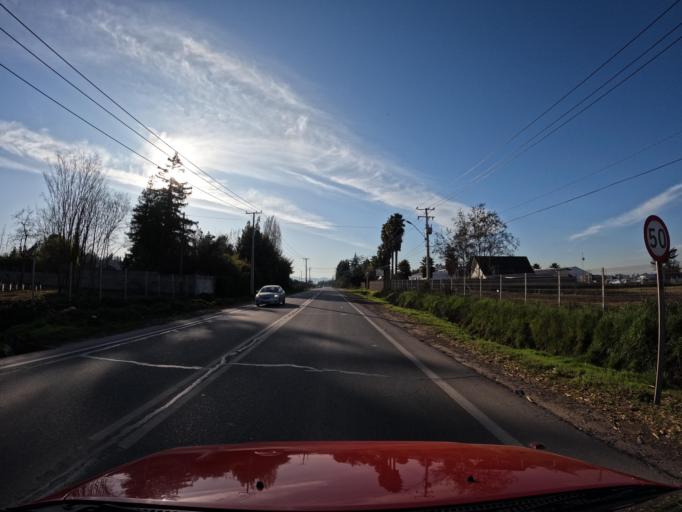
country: CL
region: Maule
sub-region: Provincia de Curico
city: Teno
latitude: -34.8622
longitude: -71.0943
